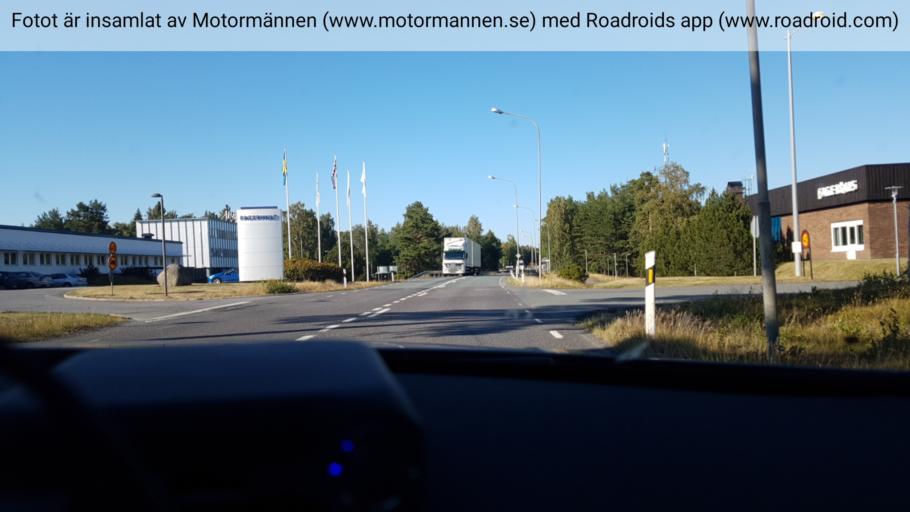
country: SE
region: Joenkoeping
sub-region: Habo Kommun
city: Habo
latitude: 57.9991
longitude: 14.1196
